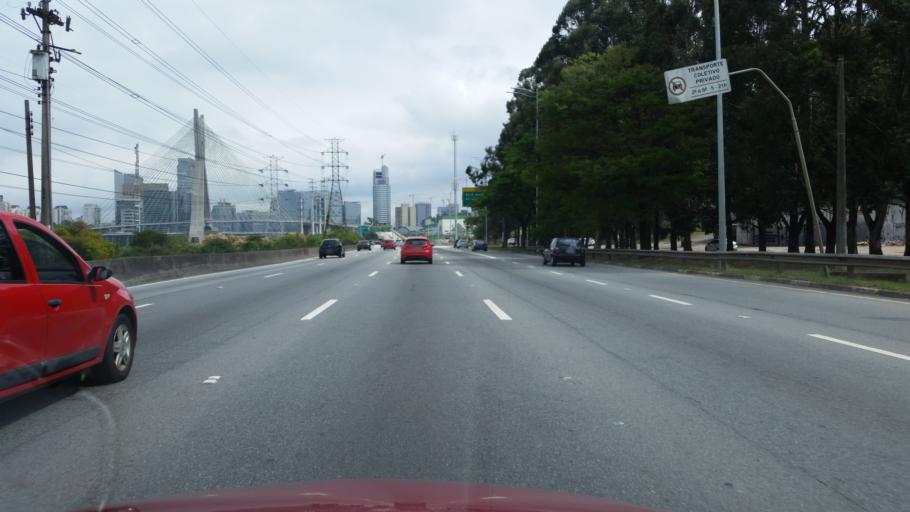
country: BR
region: Sao Paulo
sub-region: Sao Paulo
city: Sao Paulo
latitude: -23.6054
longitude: -46.6988
